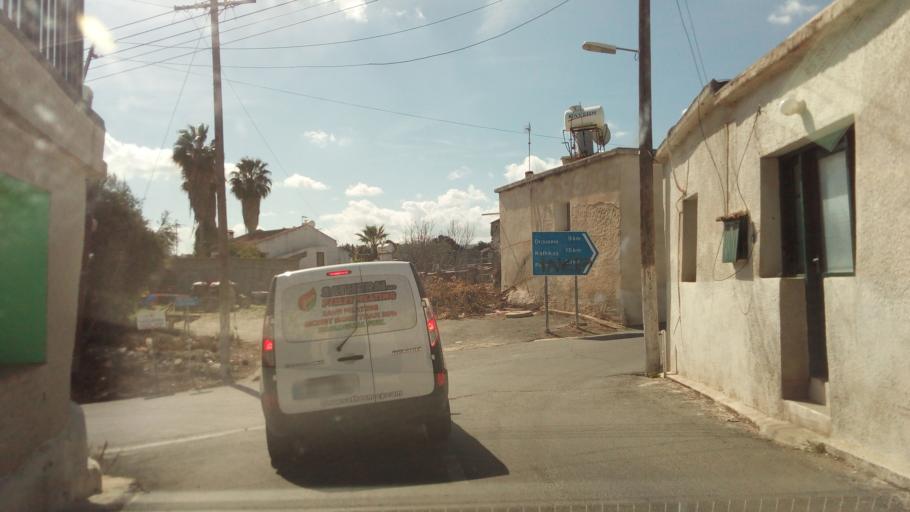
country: CY
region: Pafos
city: Polis
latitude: 35.0282
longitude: 32.4185
